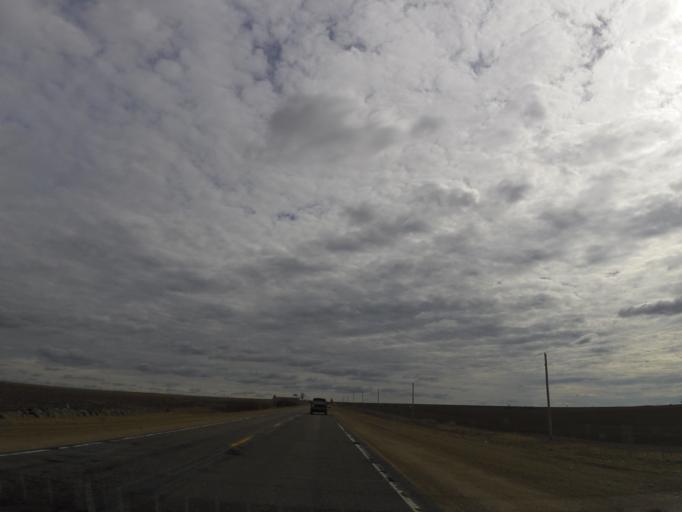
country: US
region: Iowa
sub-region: Howard County
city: Cresco
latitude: 43.3325
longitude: -92.2988
